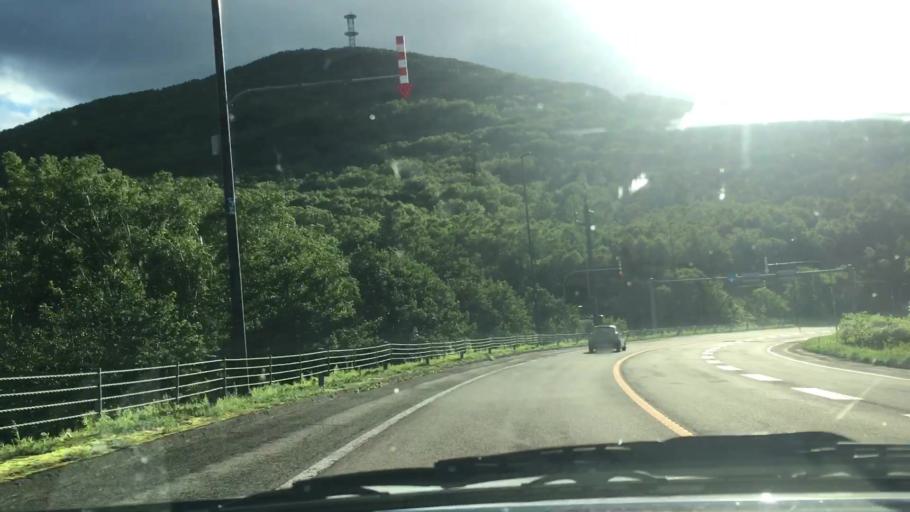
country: JP
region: Hokkaido
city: Shimo-furano
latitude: 43.1285
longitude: 142.7615
